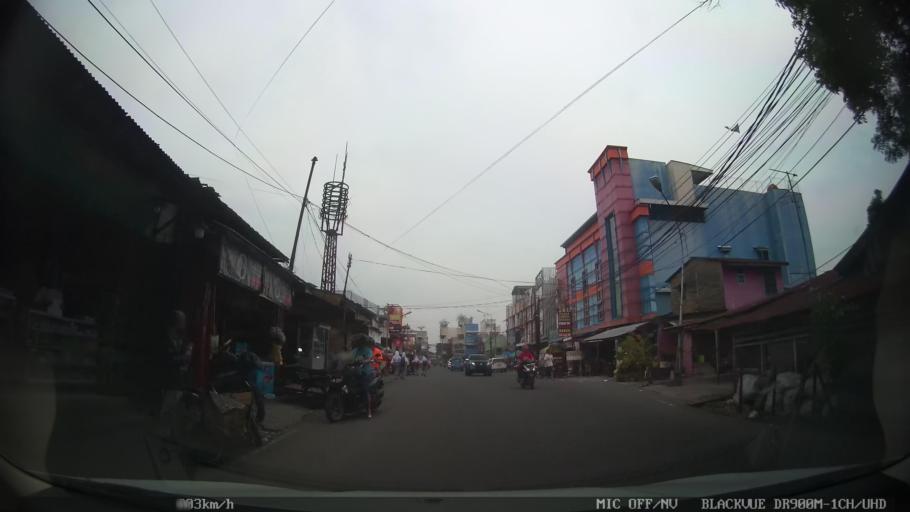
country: ID
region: North Sumatra
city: Medan
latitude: 3.5533
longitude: 98.6899
